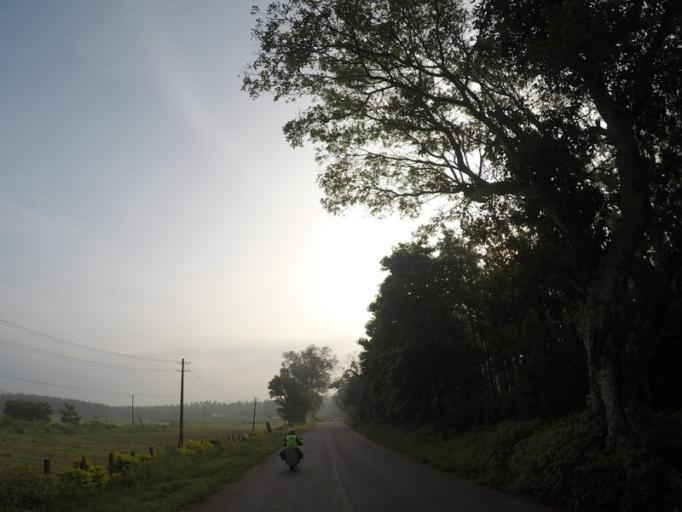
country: IN
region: Karnataka
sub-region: Chikmagalur
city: Chikmagalur
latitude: 13.4027
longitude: 75.7935
